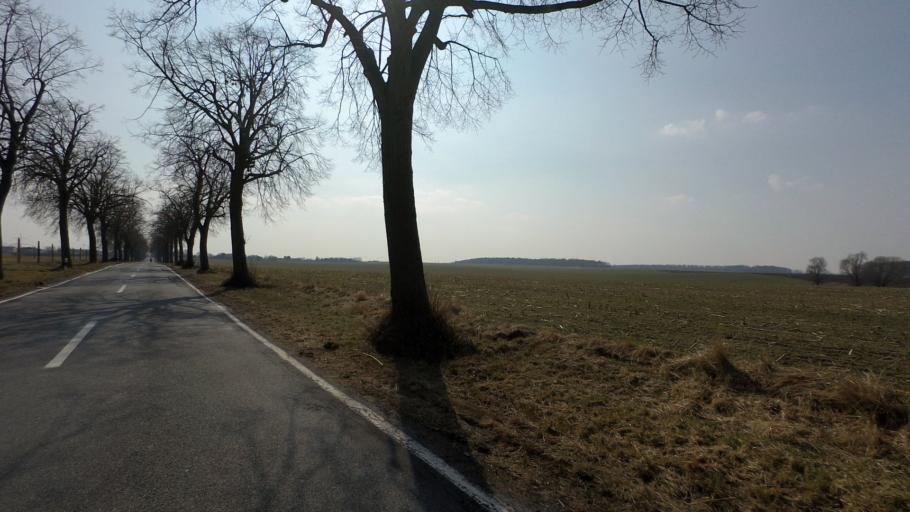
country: DE
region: Brandenburg
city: Gross Kreutz
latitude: 52.4261
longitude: 12.7882
